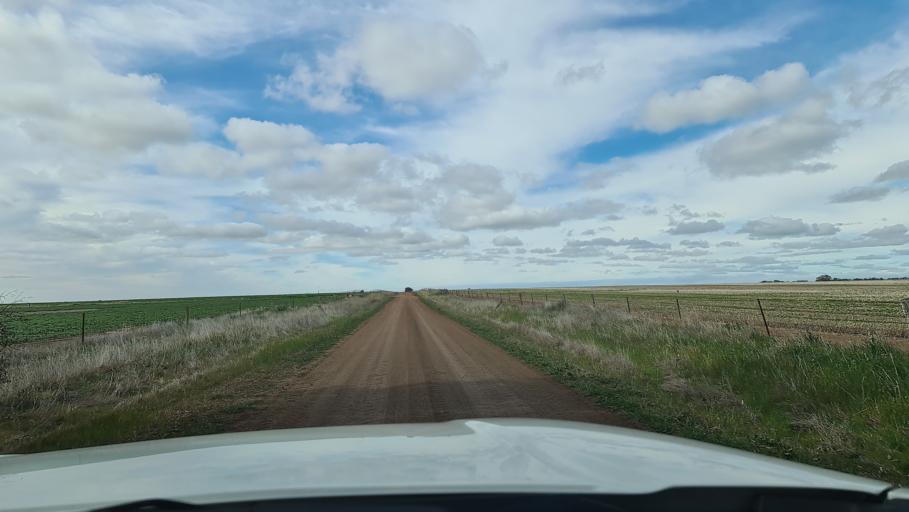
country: AU
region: Victoria
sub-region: Horsham
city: Horsham
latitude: -36.6313
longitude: 142.4172
